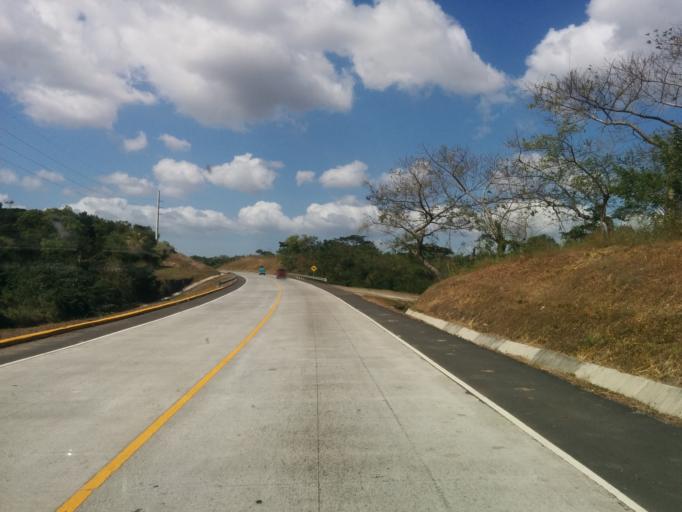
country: NI
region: Masaya
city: Masaya
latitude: 11.9891
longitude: -86.0736
